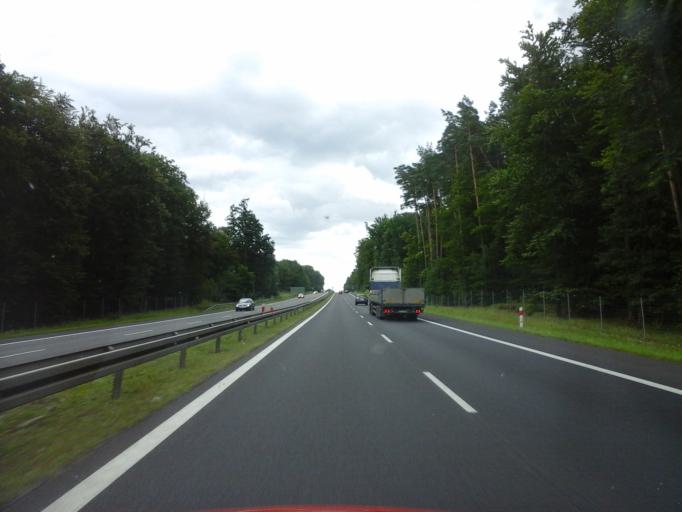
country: PL
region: West Pomeranian Voivodeship
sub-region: Powiat gryfinski
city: Stare Czarnowo
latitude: 53.3562
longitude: 14.7907
